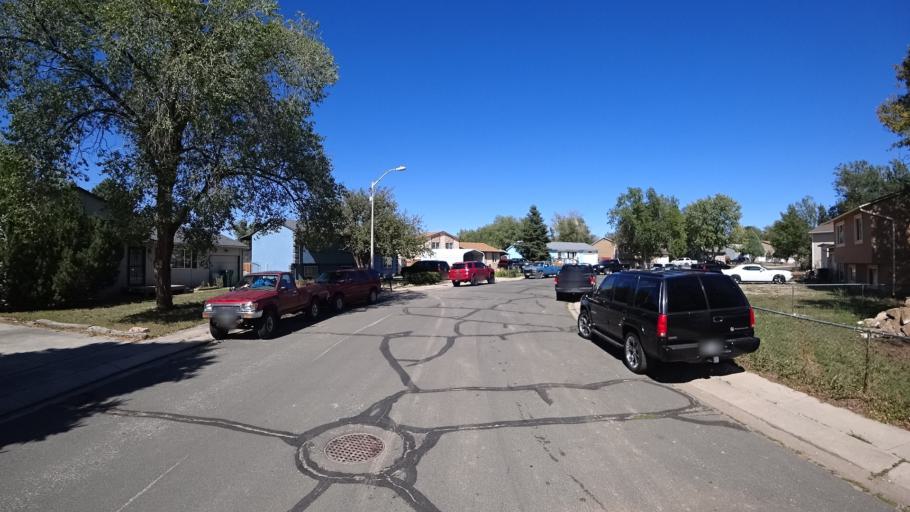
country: US
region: Colorado
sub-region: El Paso County
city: Stratmoor
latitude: 38.7828
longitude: -104.7548
